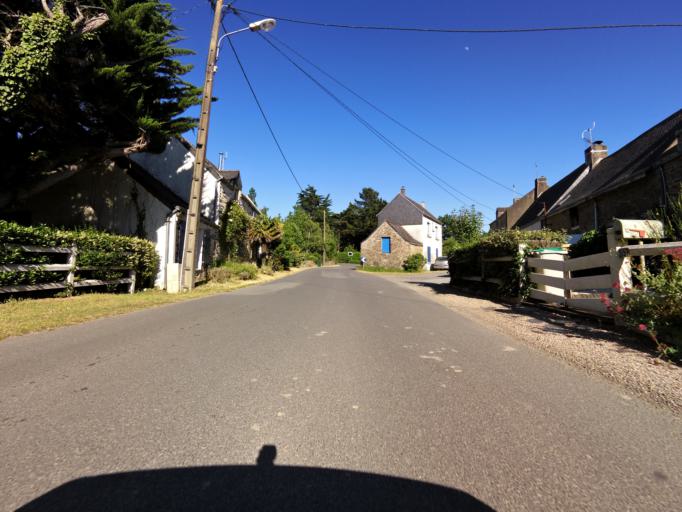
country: FR
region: Brittany
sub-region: Departement du Morbihan
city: Penestin
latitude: 47.4722
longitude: -2.4732
